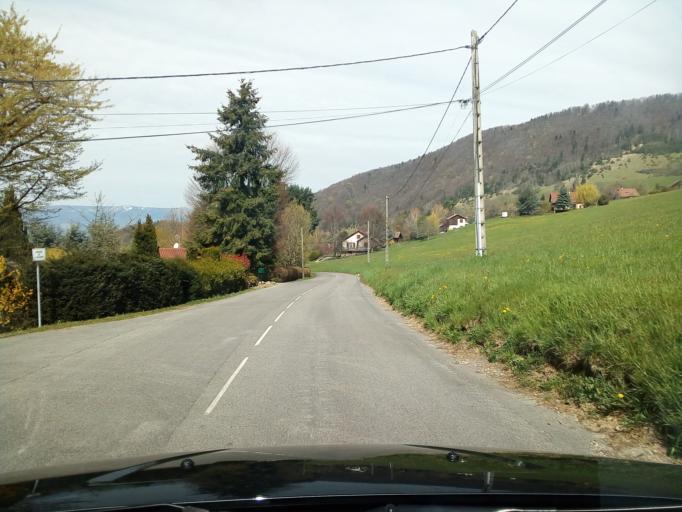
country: FR
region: Rhone-Alpes
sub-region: Departement de l'Isere
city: Revel
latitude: 45.1618
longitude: 5.8426
